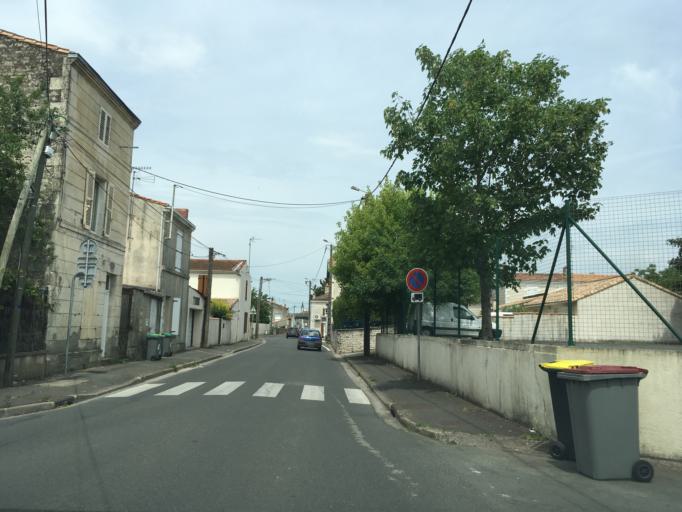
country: FR
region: Poitou-Charentes
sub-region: Departement des Deux-Sevres
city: Niort
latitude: 46.3119
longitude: -0.4620
